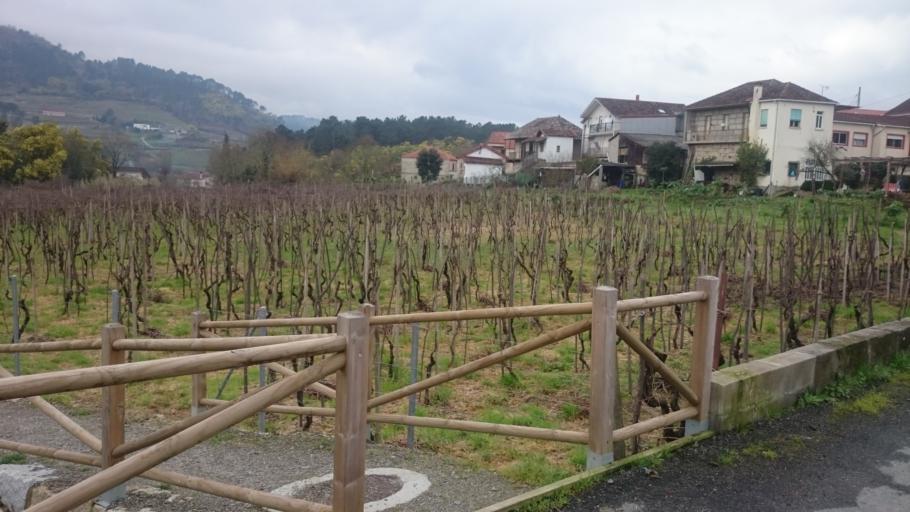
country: ES
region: Galicia
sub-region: Provincia de Ourense
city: Punxin
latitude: 42.3298
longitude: -8.0286
